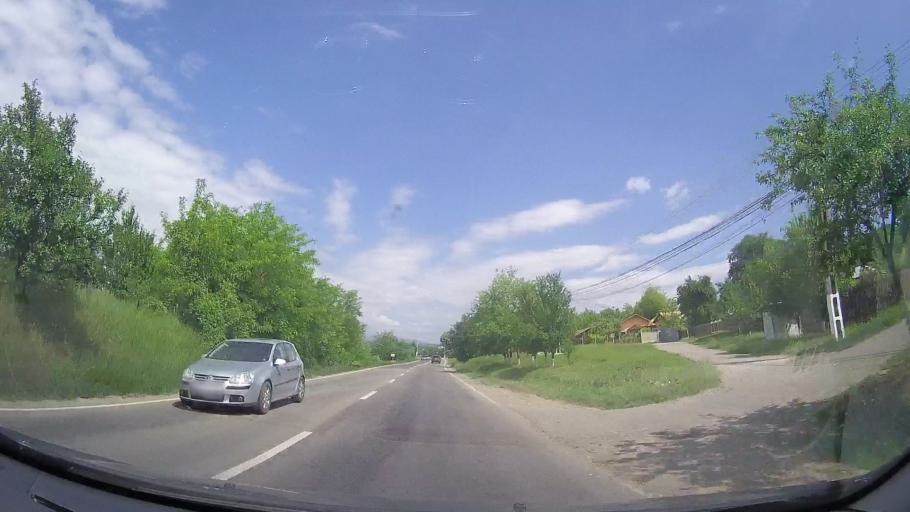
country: RO
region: Prahova
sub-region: Comuna Gura Vitioarei
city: Fagetu
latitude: 45.1269
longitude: 26.0354
